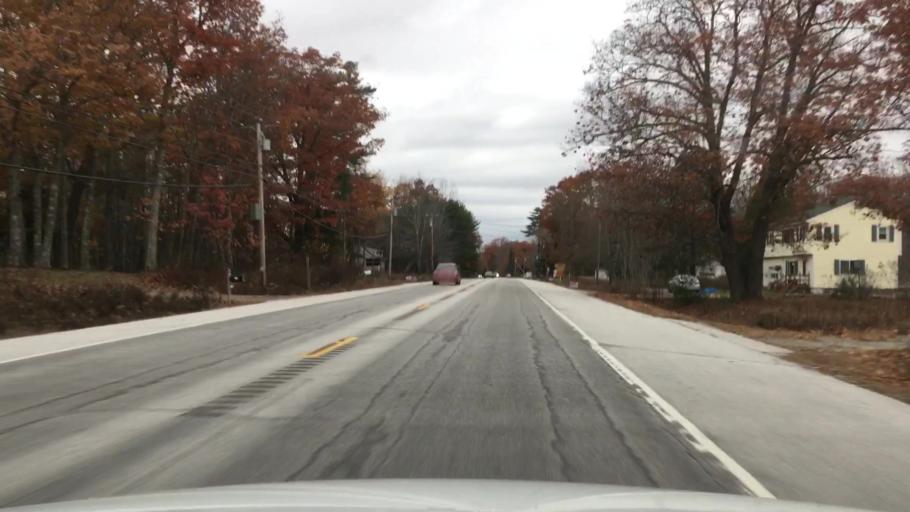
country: US
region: Maine
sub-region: Hancock County
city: Orland
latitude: 44.5634
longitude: -68.7143
